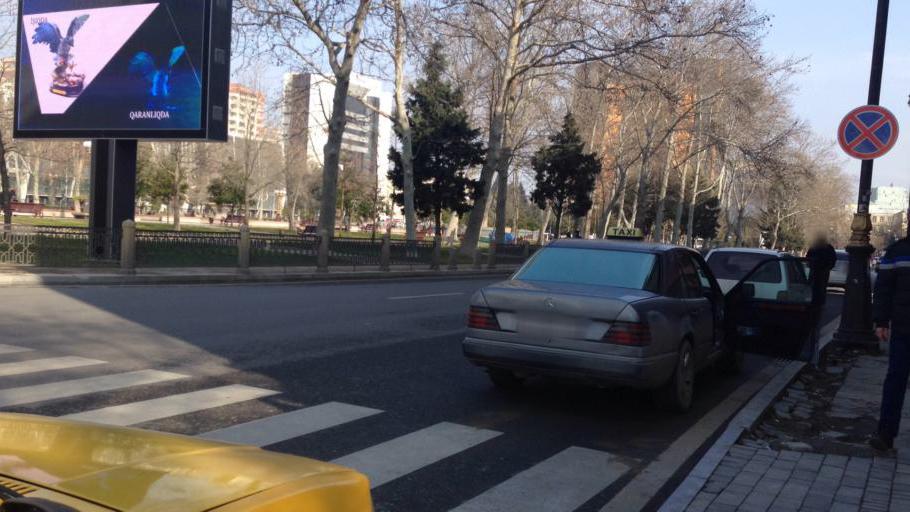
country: AZ
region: Baki
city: Baku
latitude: 40.3773
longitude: 49.8426
